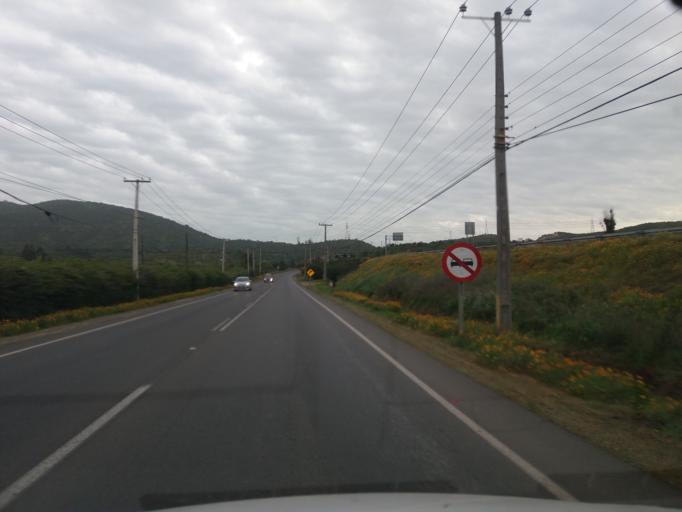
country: CL
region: Valparaiso
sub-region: Provincia de Marga Marga
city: Limache
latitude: -32.9482
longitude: -71.2850
